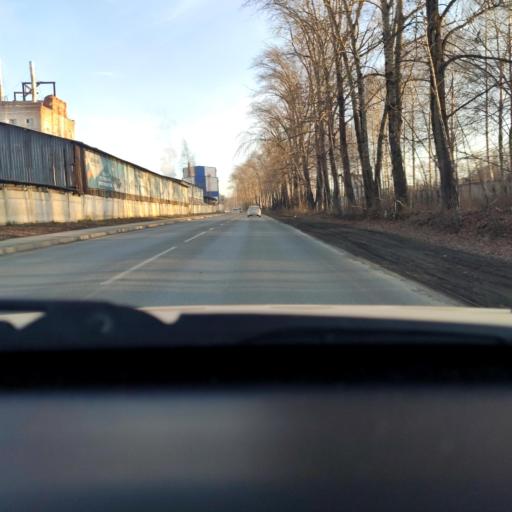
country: RU
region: Perm
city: Perm
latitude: 57.9595
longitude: 56.2079
